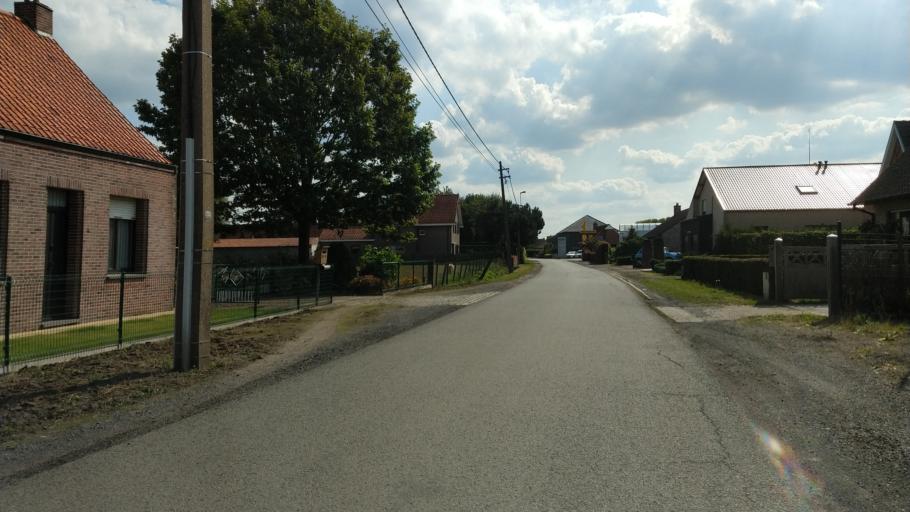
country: BE
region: Flanders
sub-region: Provincie Oost-Vlaanderen
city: Kaprijke
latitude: 51.1956
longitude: 3.6796
